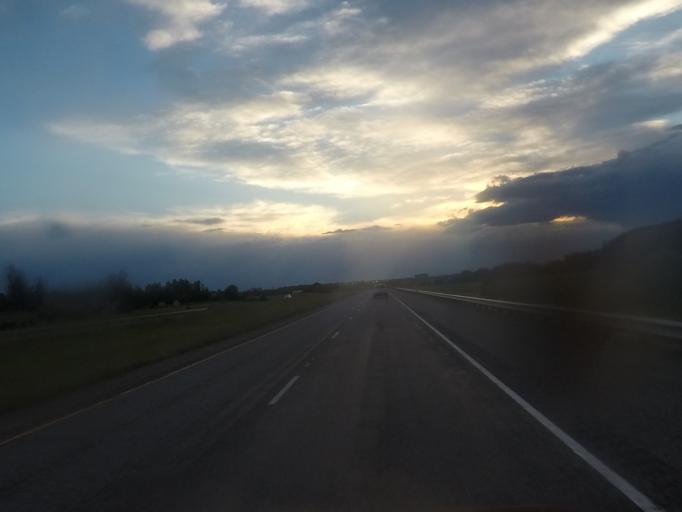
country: US
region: Montana
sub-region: Gallatin County
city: Bozeman
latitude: 45.6668
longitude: -110.9822
